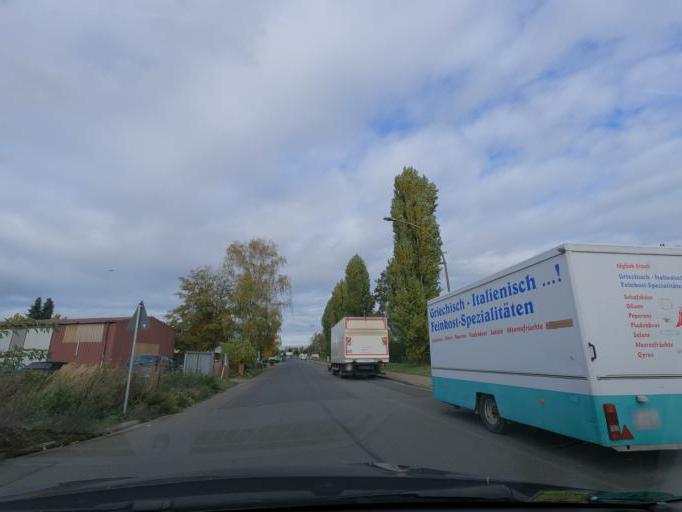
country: DE
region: Lower Saxony
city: Leiferde
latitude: 52.2115
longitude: 10.4978
